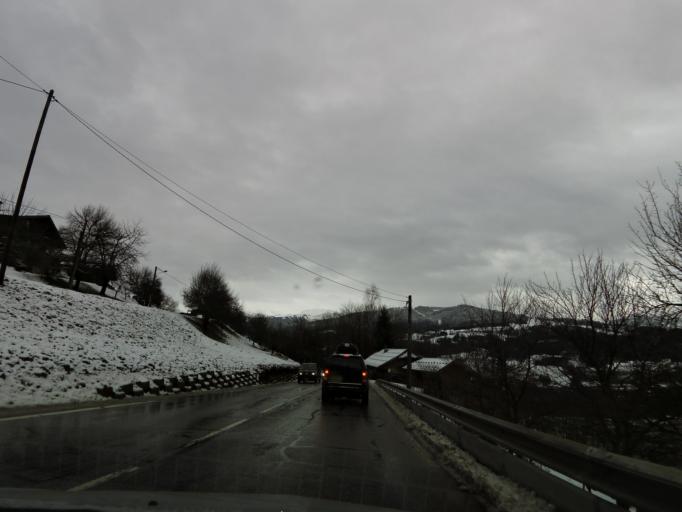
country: FR
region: Rhone-Alpes
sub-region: Departement de la Haute-Savoie
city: Taninges
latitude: 46.1123
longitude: 6.6086
